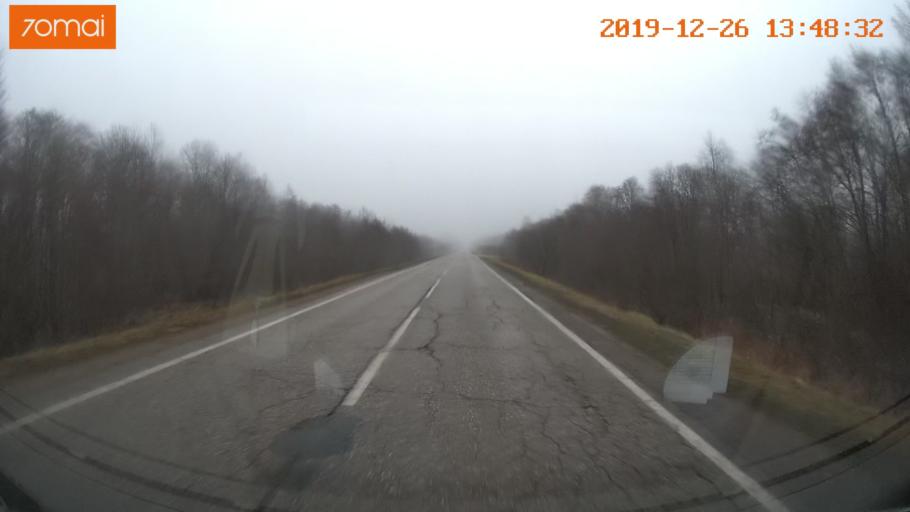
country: RU
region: Vologda
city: Sheksna
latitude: 58.6755
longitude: 38.5487
